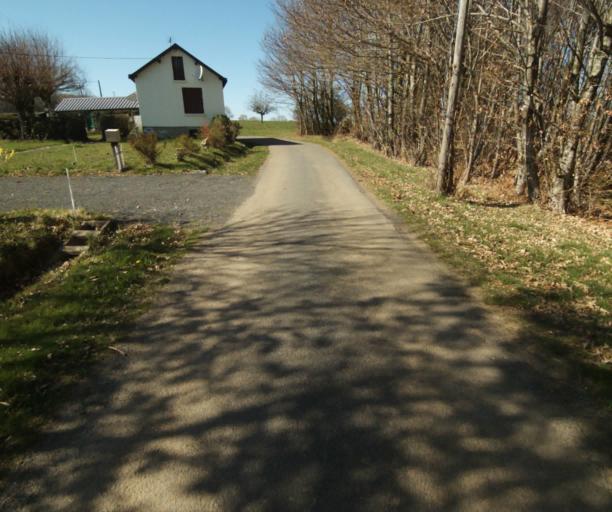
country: FR
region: Limousin
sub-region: Departement de la Correze
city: Chamboulive
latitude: 45.4101
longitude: 1.6484
